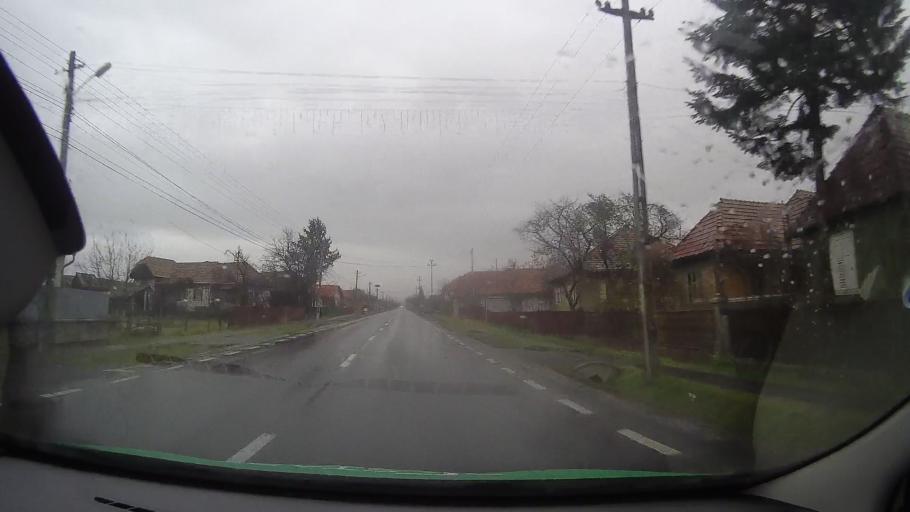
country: RO
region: Mures
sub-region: Comuna Alunis
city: Alunis
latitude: 46.8968
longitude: 24.8045
